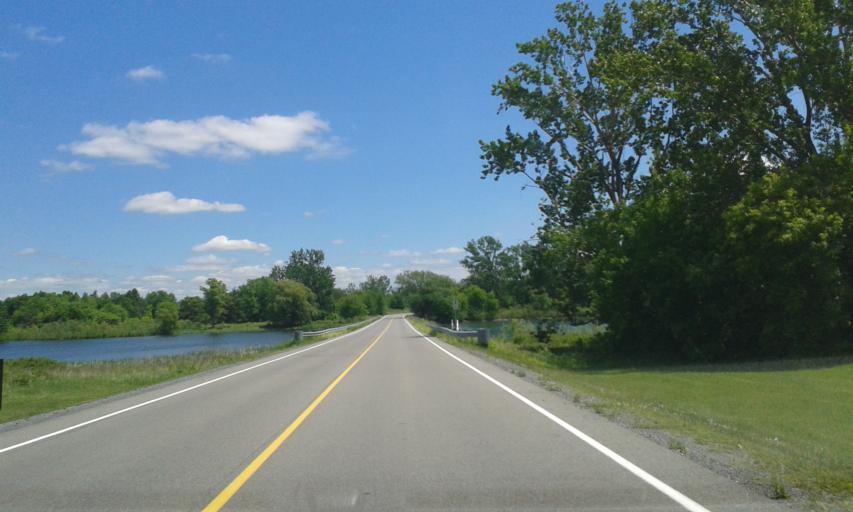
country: US
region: New York
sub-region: St. Lawrence County
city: Massena
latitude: 44.9964
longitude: -74.9181
